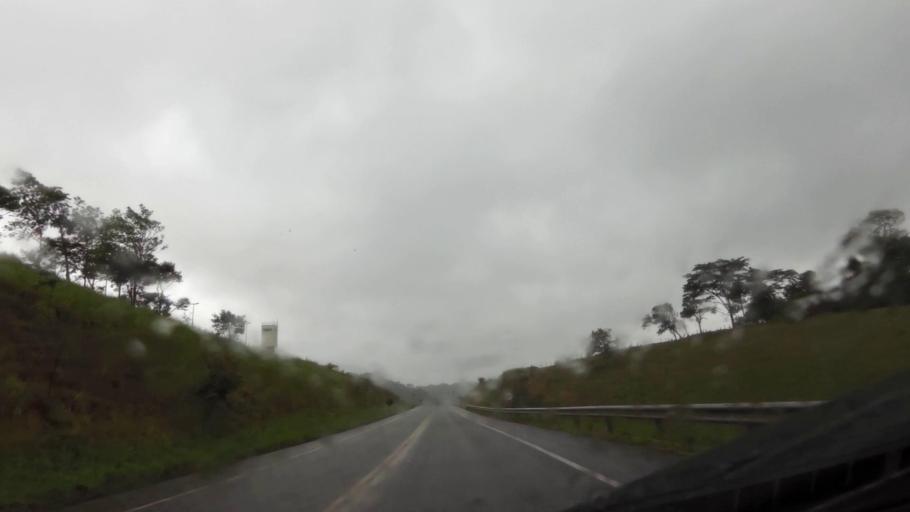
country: BR
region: Espirito Santo
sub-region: Guarapari
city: Guarapari
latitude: -20.6403
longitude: -40.5307
